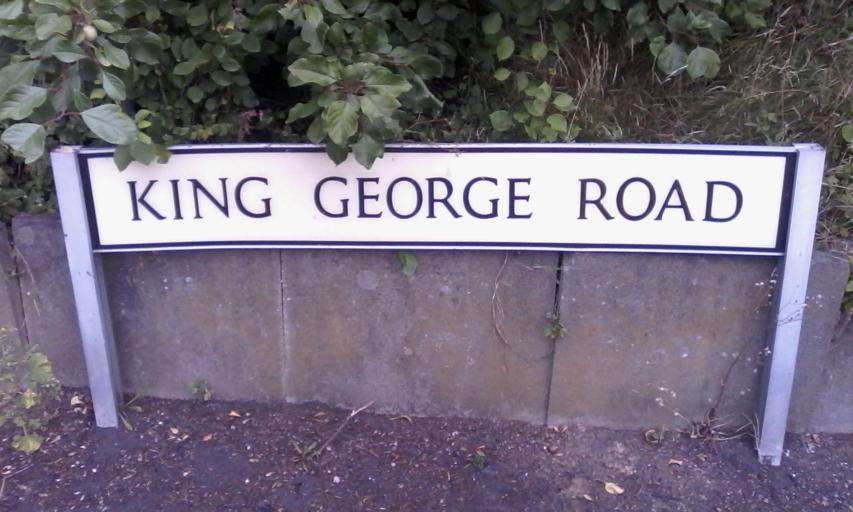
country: GB
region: England
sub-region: Hertfordshire
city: Ware
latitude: 51.8129
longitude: -0.0240
